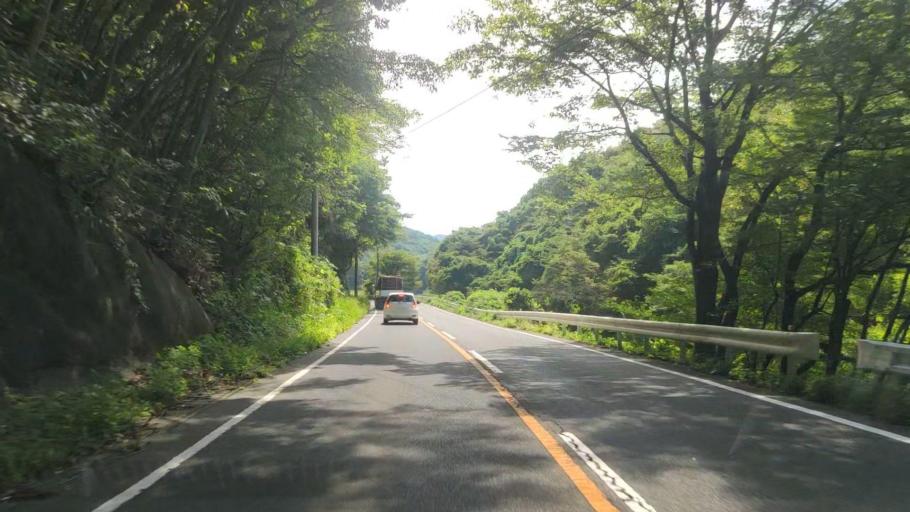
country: JP
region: Gunma
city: Numata
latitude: 36.6320
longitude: 138.9936
